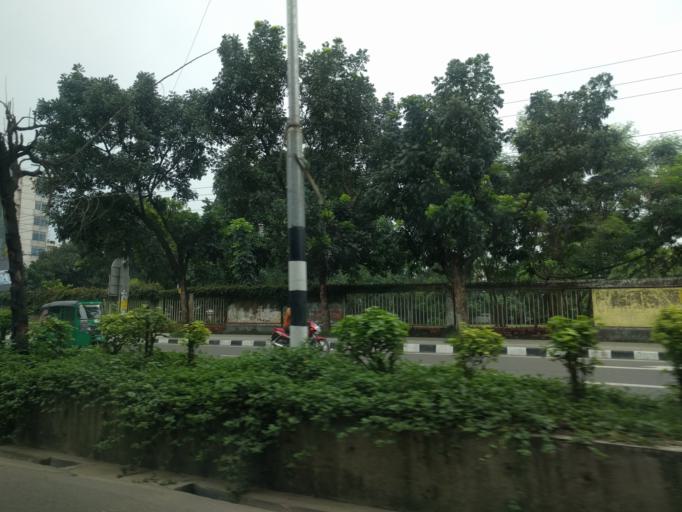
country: BD
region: Dhaka
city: Paltan
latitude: 23.7911
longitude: 90.4158
